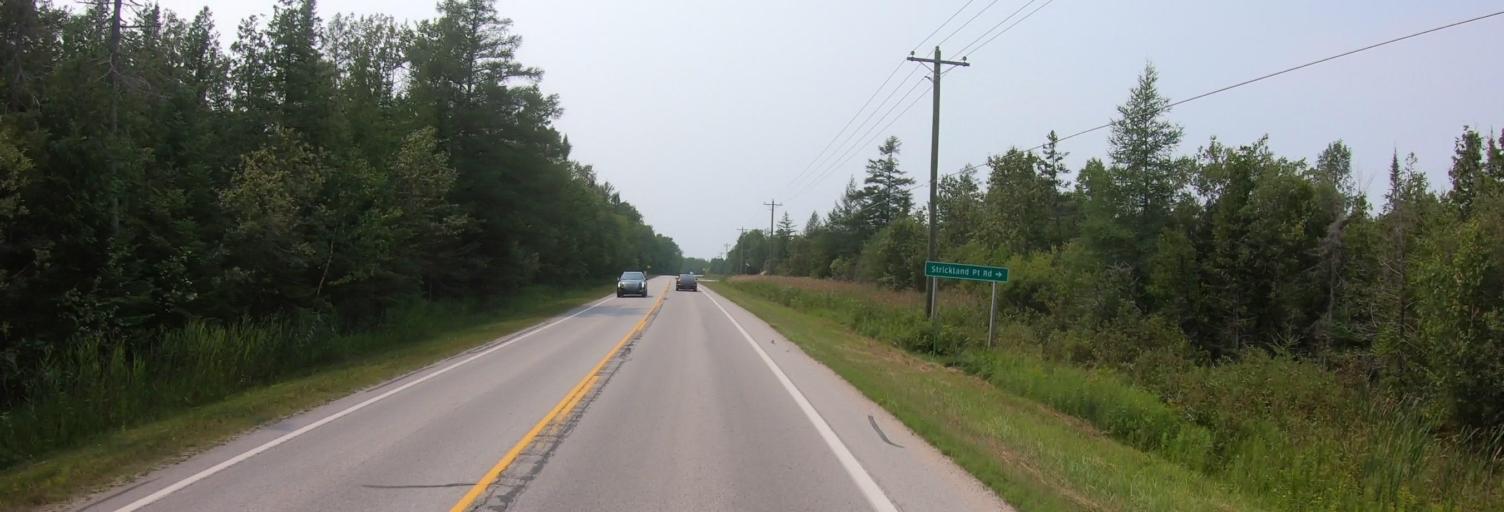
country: CA
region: Ontario
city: Thessalon
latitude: 45.9994
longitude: -83.7670
